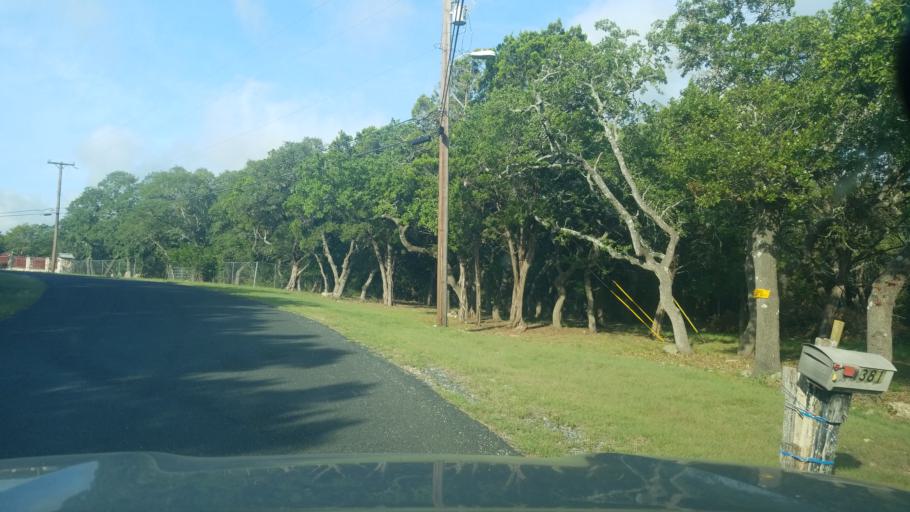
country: US
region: Texas
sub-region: Bexar County
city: Timberwood Park
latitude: 29.7053
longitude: -98.5188
